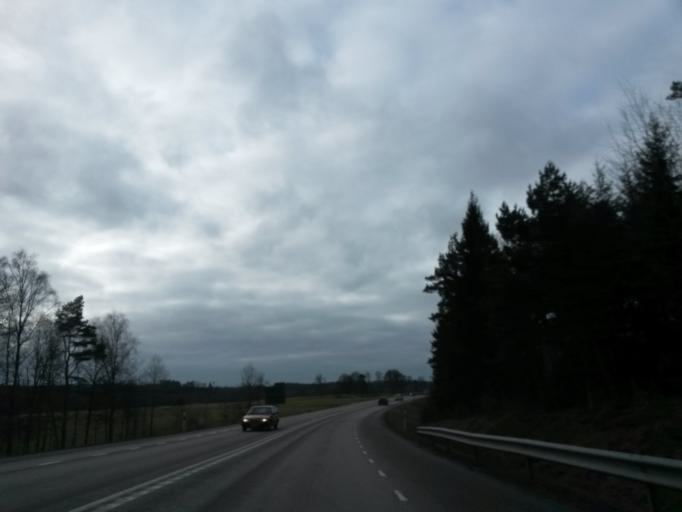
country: SE
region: Vaestra Goetaland
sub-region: Vargarda Kommun
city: Jonstorp
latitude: 57.9779
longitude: 12.6820
